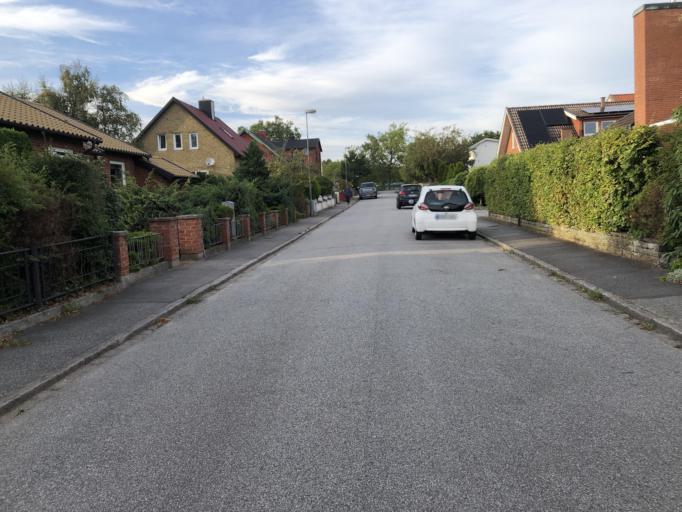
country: SE
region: Skane
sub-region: Burlovs Kommun
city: Arloev
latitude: 55.5935
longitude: 13.0695
